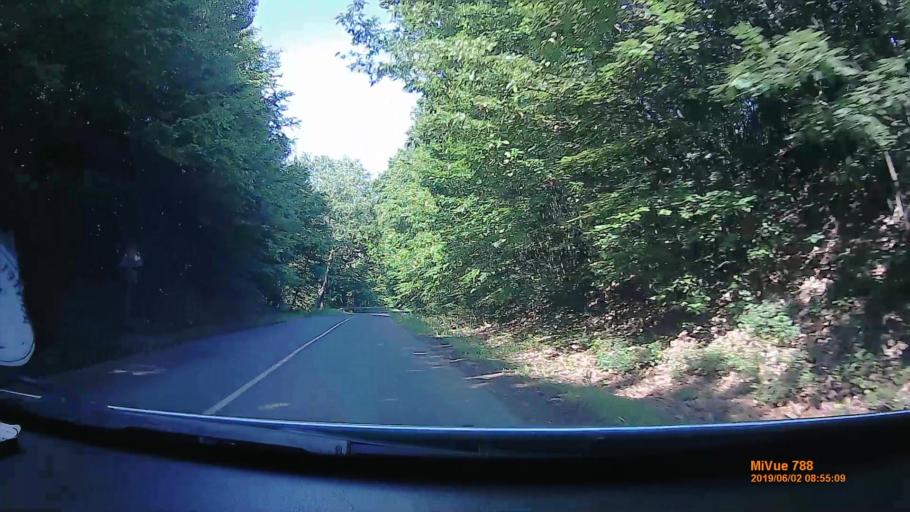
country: HU
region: Borsod-Abauj-Zemplen
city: Sajobabony
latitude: 48.1541
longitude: 20.6652
